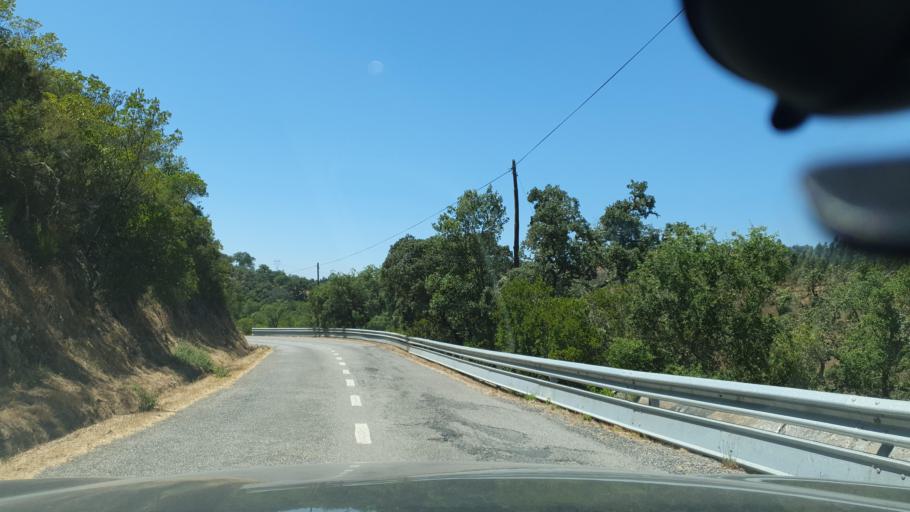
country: PT
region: Beja
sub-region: Odemira
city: Odemira
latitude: 37.6042
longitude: -8.5742
